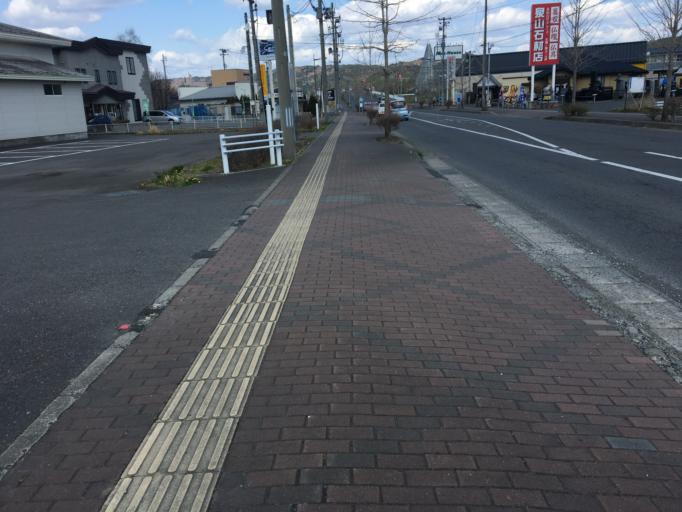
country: JP
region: Aomori
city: Hachinohe
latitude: 40.1880
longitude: 141.7813
